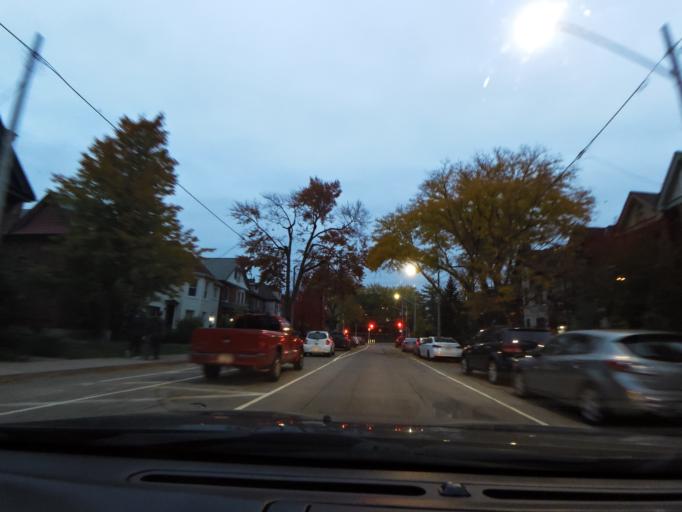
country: CA
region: Ontario
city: Hamilton
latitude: 43.2517
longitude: -79.8832
